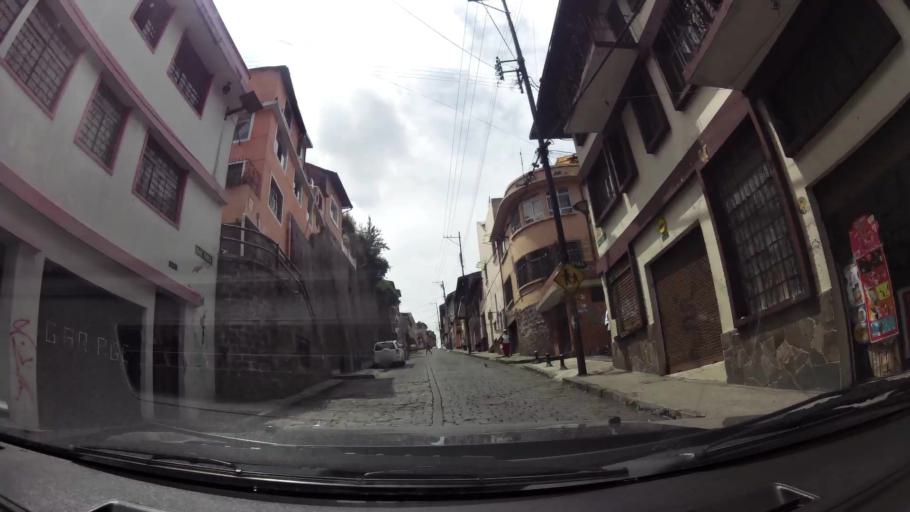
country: EC
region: Pichincha
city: Quito
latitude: -0.2158
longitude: -78.5113
